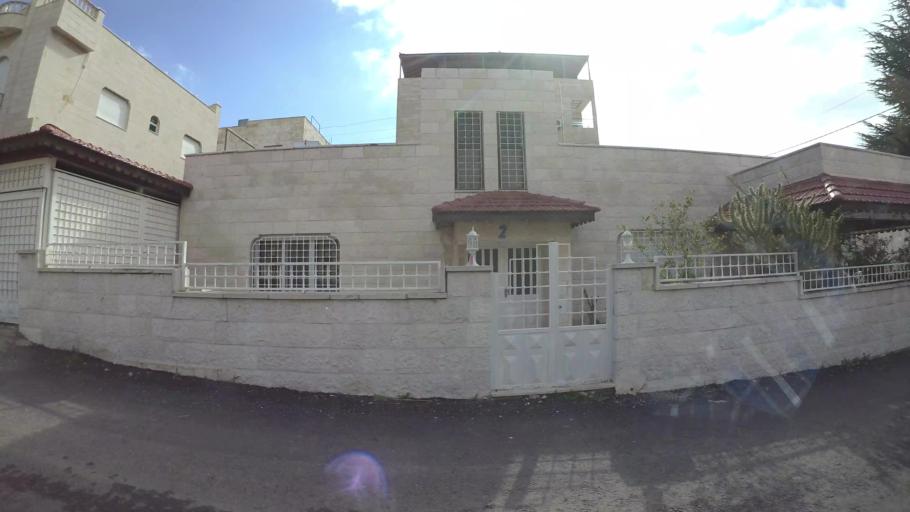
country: JO
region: Amman
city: Wadi as Sir
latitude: 31.9485
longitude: 35.8458
